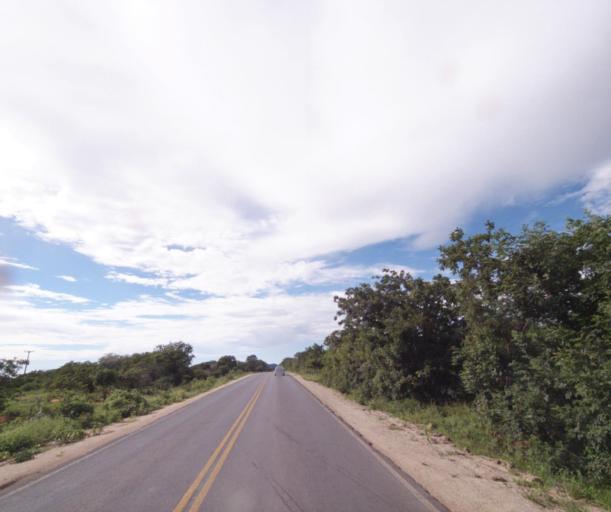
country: BR
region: Bahia
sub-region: Guanambi
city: Guanambi
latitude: -14.4295
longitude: -42.7262
